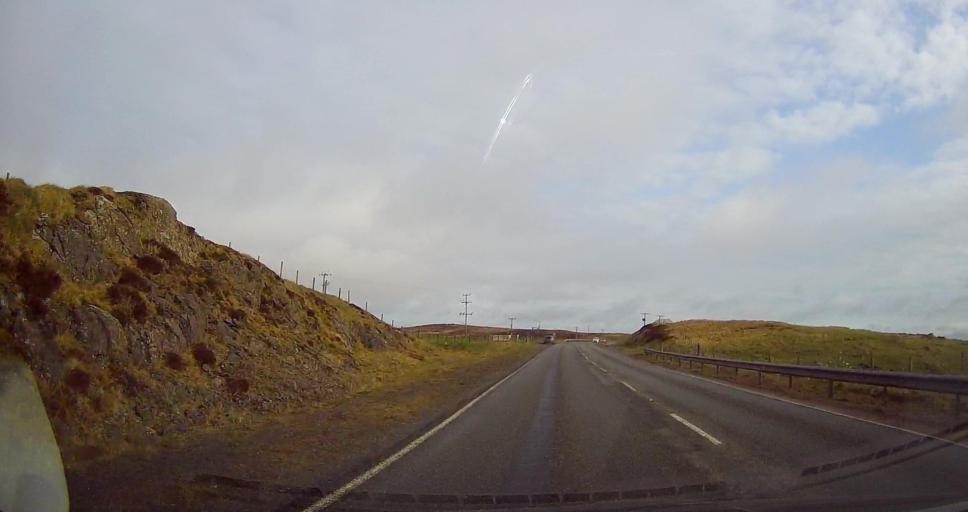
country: GB
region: Scotland
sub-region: Shetland Islands
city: Lerwick
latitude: 60.1115
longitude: -1.2191
